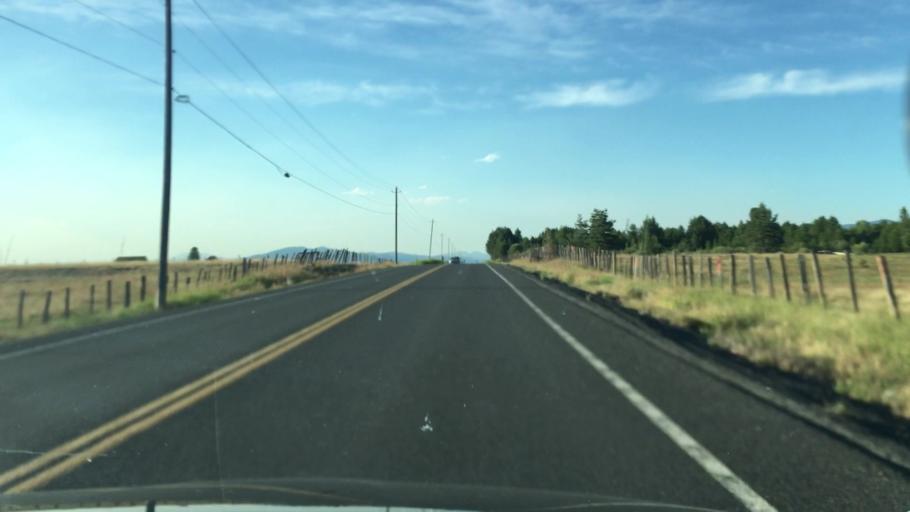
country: US
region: Idaho
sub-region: Valley County
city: McCall
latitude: 44.7982
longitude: -116.0782
